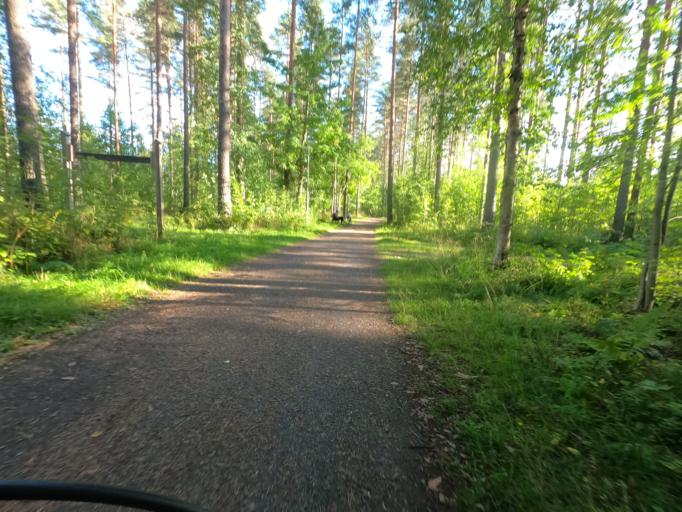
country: FI
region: North Karelia
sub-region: Joensuu
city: Joensuu
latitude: 62.6145
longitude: 29.7526
